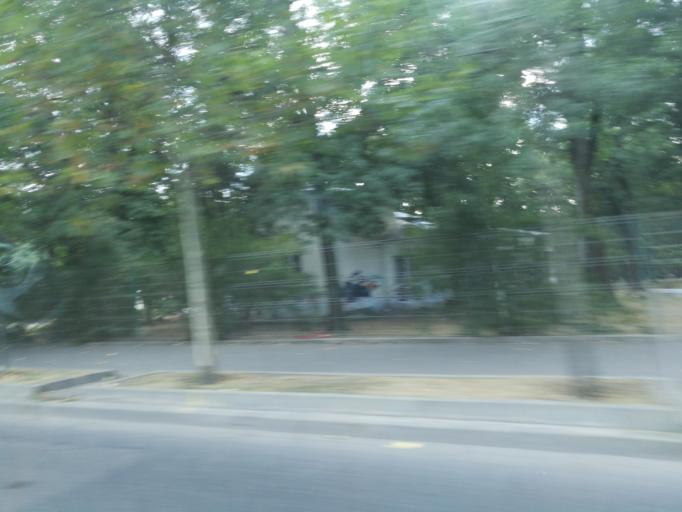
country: RO
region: Ilfov
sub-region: Comuna Chiajna
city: Rosu
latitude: 44.4897
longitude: 26.0355
